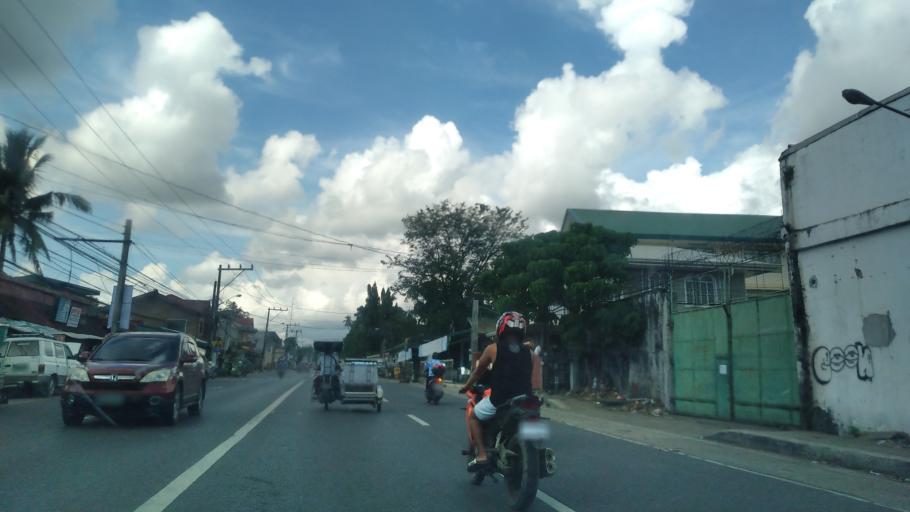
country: PH
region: Calabarzon
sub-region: Province of Quezon
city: Isabang
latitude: 13.9494
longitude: 121.5817
